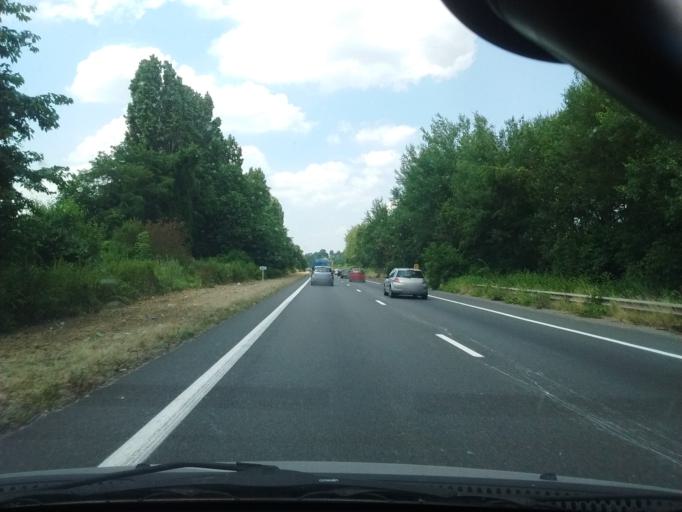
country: FR
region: Ile-de-France
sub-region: Departement de l'Essonne
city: Tigery
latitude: 48.6316
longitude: 2.5064
